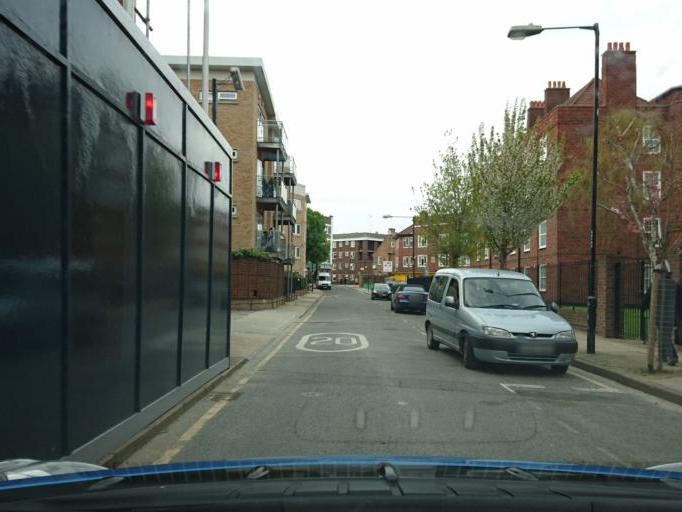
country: GB
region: England
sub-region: Greater London
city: Bethnal Green
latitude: 51.5322
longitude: -0.0648
